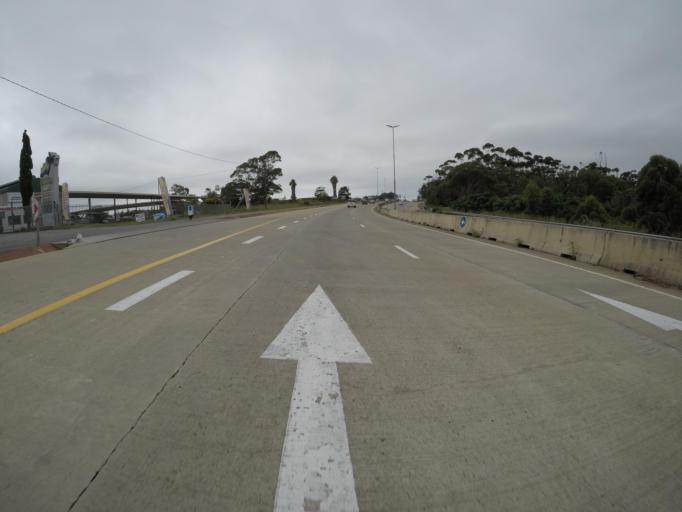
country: ZA
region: Eastern Cape
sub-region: Buffalo City Metropolitan Municipality
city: East London
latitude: -32.9396
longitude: 27.9590
